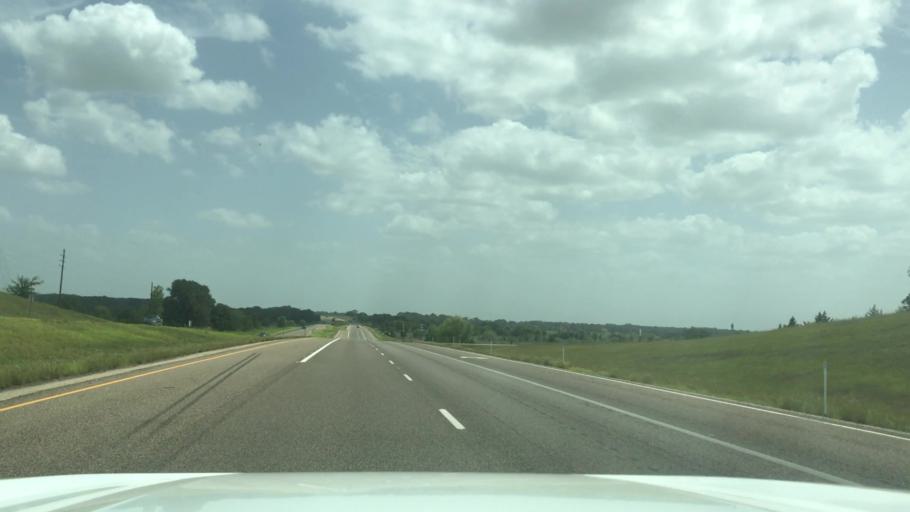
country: US
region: Texas
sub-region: Robertson County
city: Calvert
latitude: 31.0223
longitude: -96.7081
